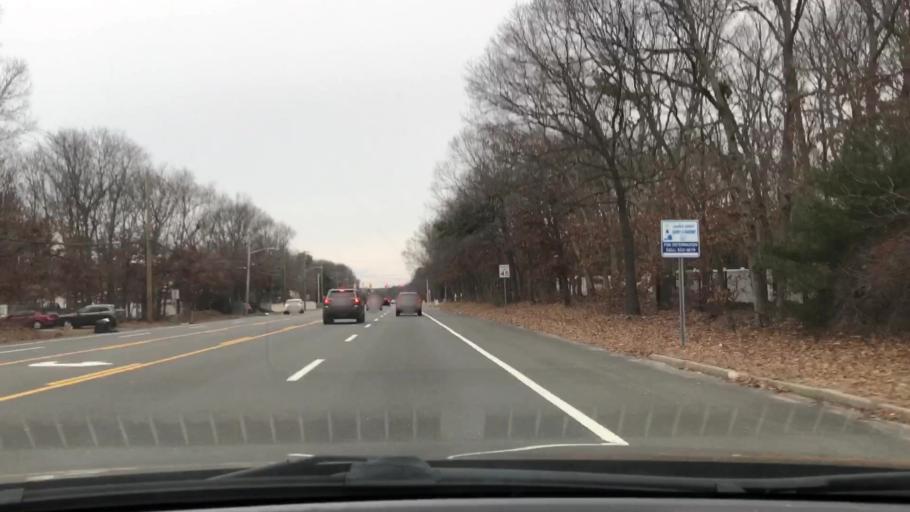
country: US
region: New York
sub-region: Suffolk County
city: North Patchogue
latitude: 40.7996
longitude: -73.0177
